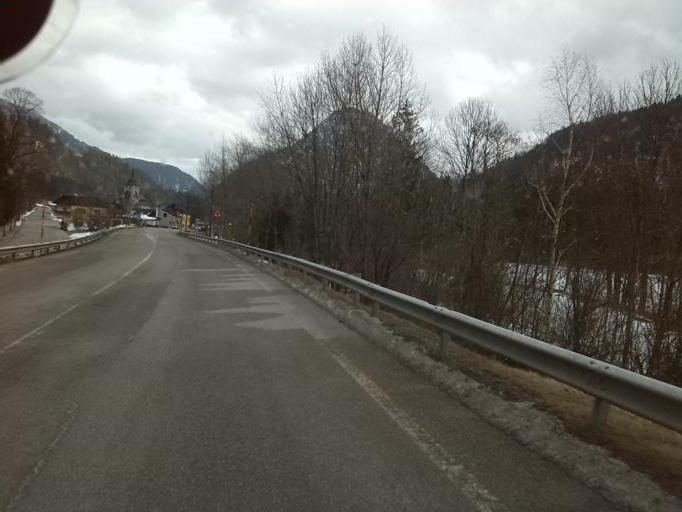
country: IT
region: Friuli Venezia Giulia
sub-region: Provincia di Udine
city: Malborghetto
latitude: 46.5061
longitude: 13.4375
